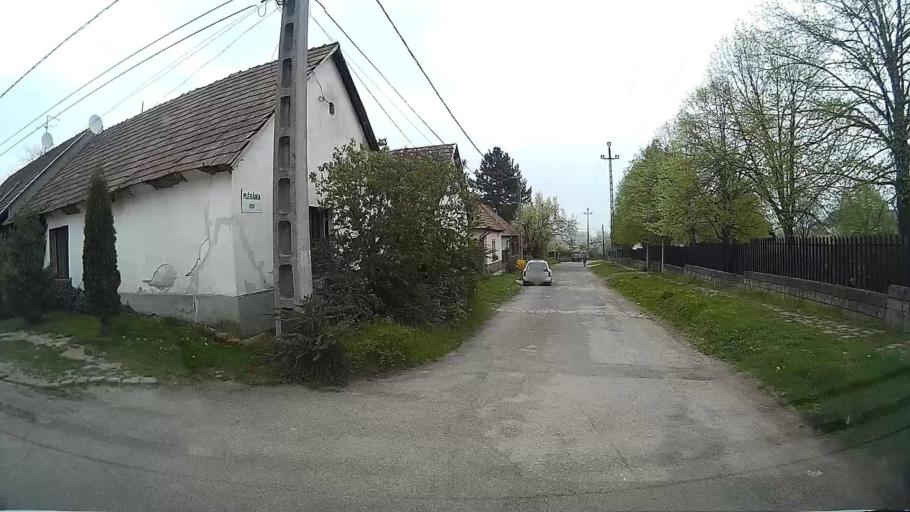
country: HU
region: Pest
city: Dunabogdany
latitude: 47.7901
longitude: 19.0337
